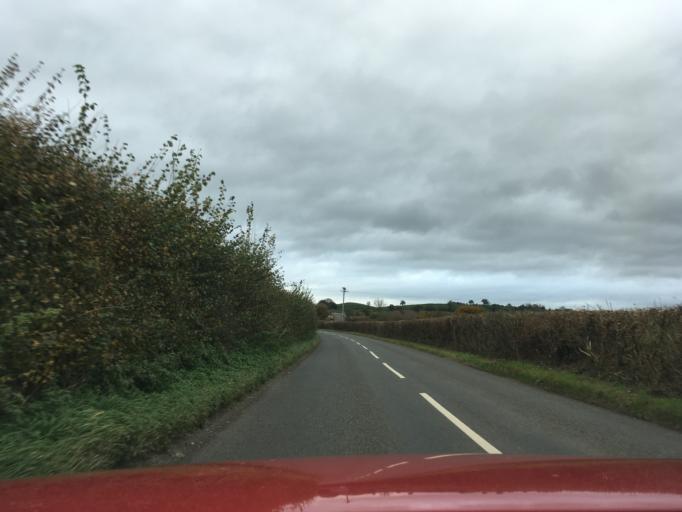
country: GB
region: England
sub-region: Somerset
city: Ilminster
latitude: 50.9530
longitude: -2.9011
